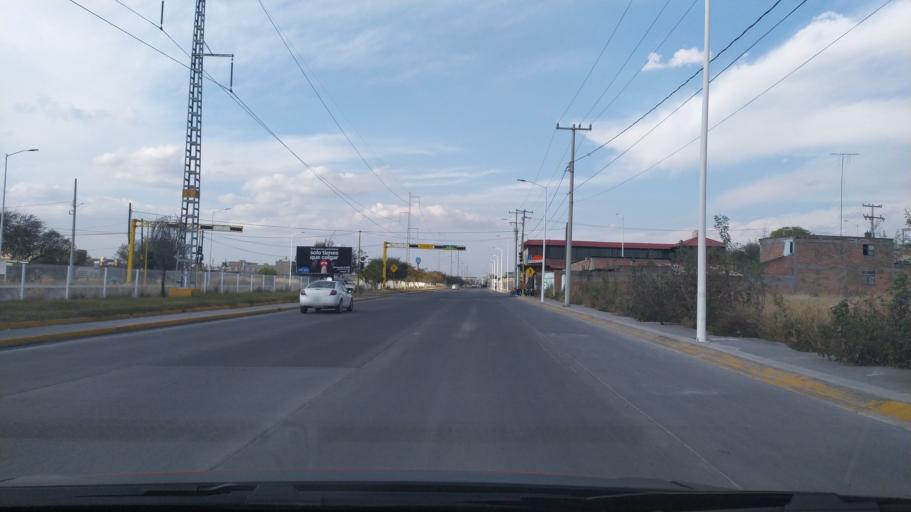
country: MX
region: Guanajuato
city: San Francisco del Rincon
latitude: 21.0133
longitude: -101.8698
